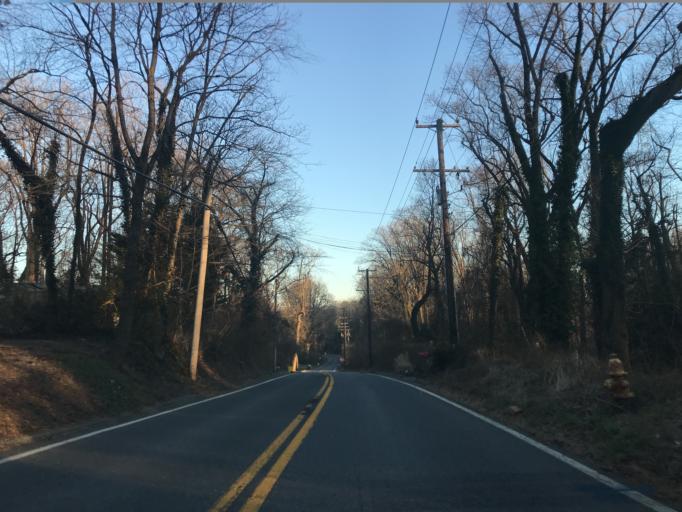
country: US
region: Maryland
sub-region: Anne Arundel County
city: Naval Academy
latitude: 39.0044
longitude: -76.4808
